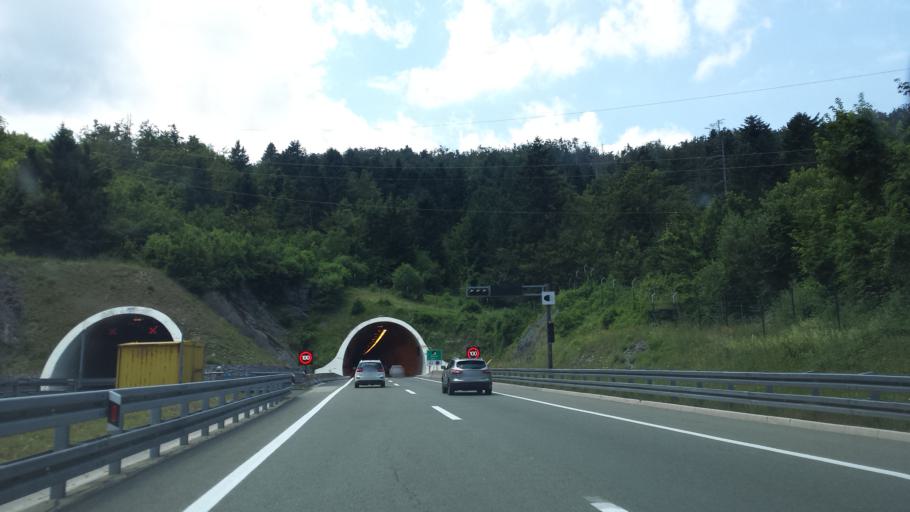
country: HR
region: Primorsko-Goranska
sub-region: Grad Delnice
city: Delnice
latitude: 45.3465
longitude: 14.7542
